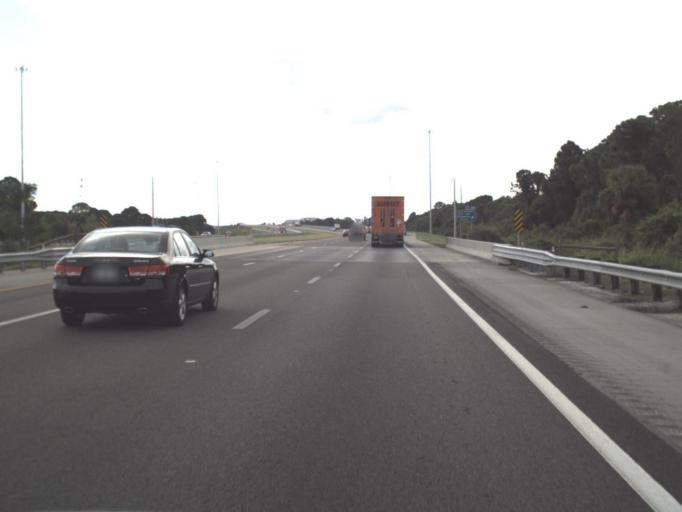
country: US
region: Florida
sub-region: Sarasota County
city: Venice Gardens
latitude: 27.1170
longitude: -82.3919
